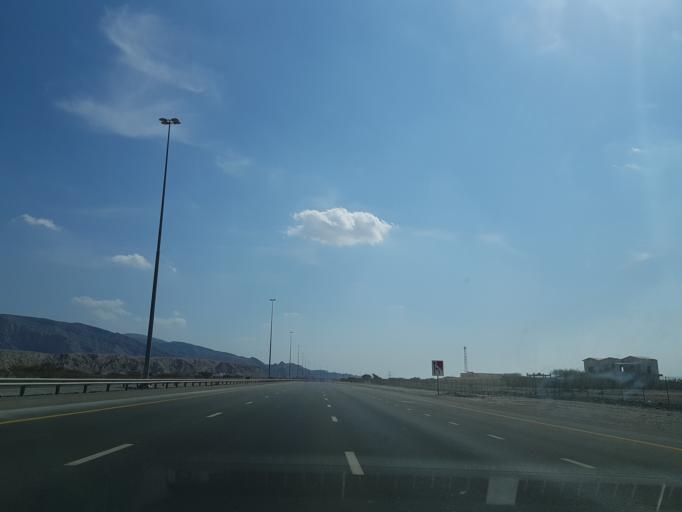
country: AE
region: Ra's al Khaymah
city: Ras al-Khaimah
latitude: 25.7938
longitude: 56.0309
